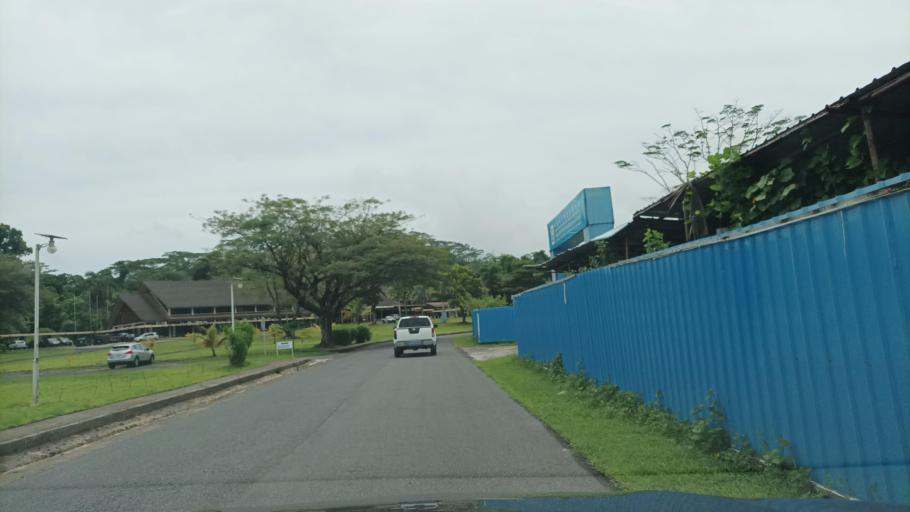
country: FM
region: Pohnpei
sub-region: Sokehs Municipality
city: Palikir - National Government Center
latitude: 6.9240
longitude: 158.1608
